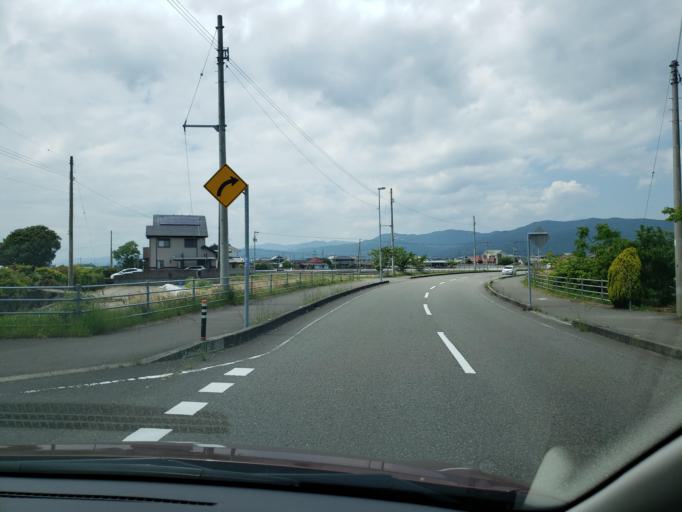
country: JP
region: Tokushima
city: Kamojimacho-jogejima
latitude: 34.0962
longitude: 134.3814
